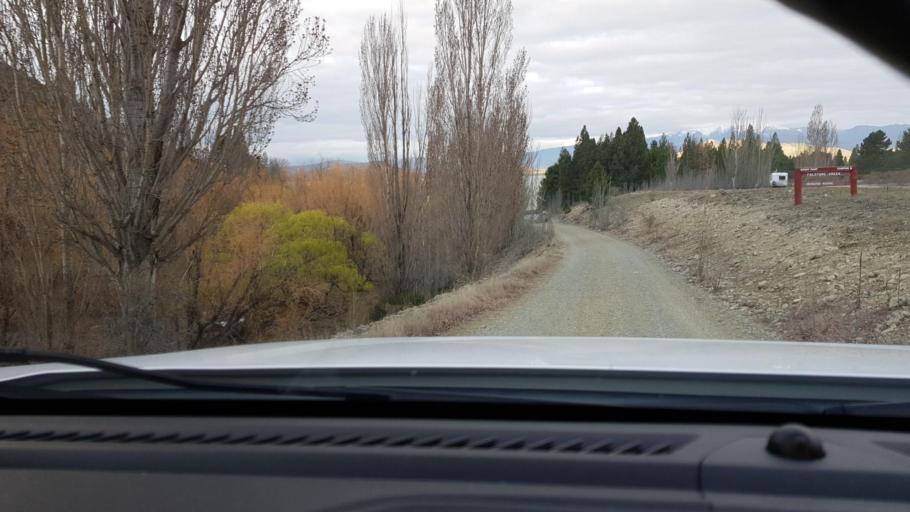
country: NZ
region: Canterbury
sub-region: Timaru District
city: Pleasant Point
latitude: -44.3981
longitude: 170.1966
